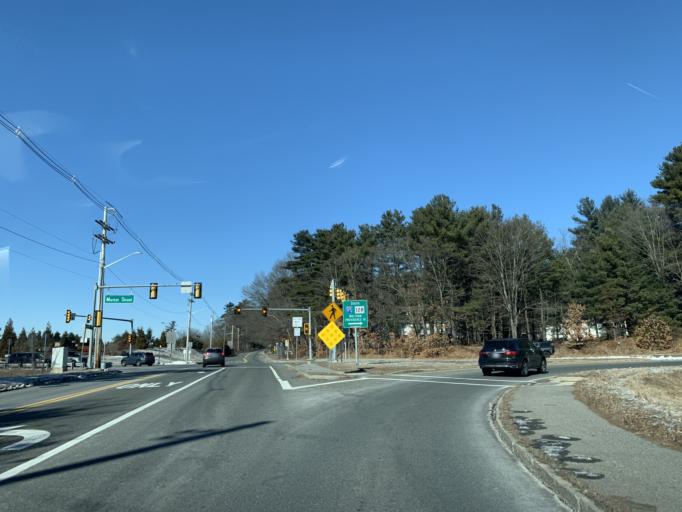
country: US
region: Massachusetts
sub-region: Essex County
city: Lynnfield
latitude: 42.5145
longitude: -71.0292
